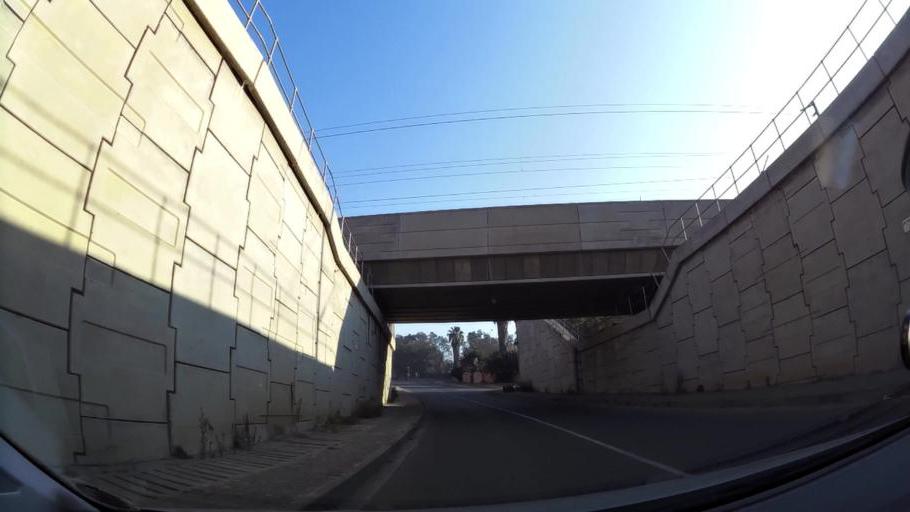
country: ZA
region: Gauteng
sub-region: City of Johannesburg Metropolitan Municipality
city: Modderfontein
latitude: -26.0851
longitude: 28.1040
